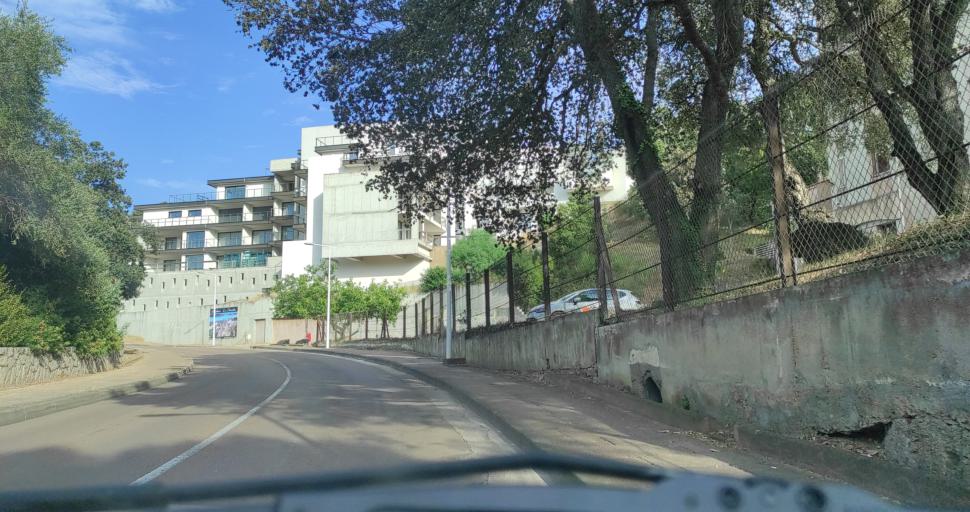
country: FR
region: Corsica
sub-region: Departement de la Corse-du-Sud
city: Porto-Vecchio
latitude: 41.5947
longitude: 9.2761
